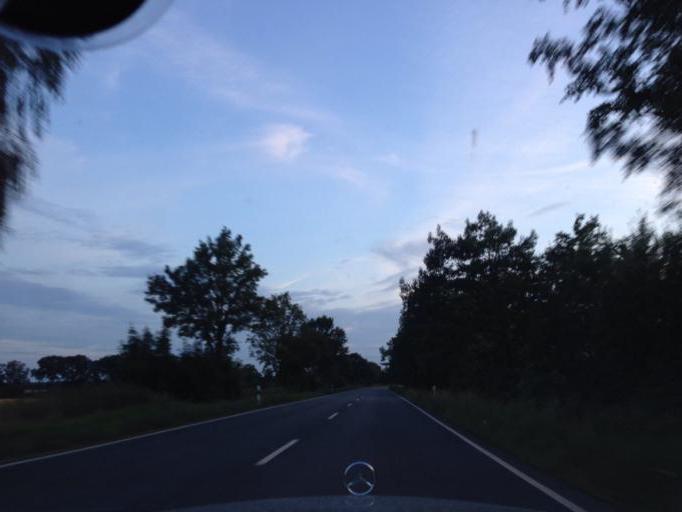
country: DE
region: Schleswig-Holstein
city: Grosshansdorf
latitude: 53.6862
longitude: 10.2748
